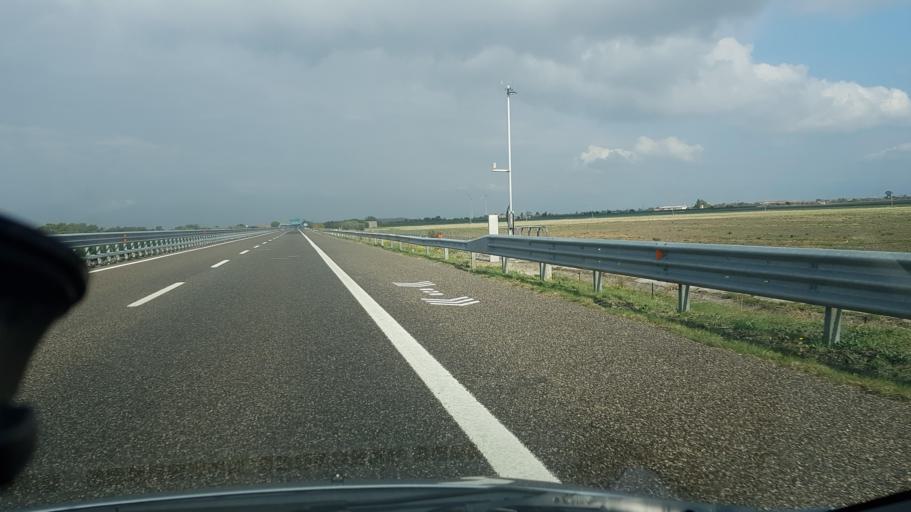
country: IT
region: Apulia
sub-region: Provincia di Foggia
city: Carapelle
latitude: 41.4146
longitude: 15.6668
